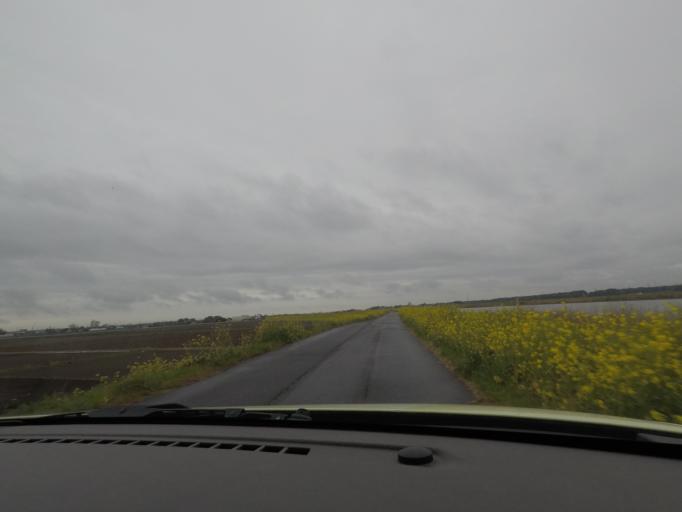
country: JP
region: Ibaraki
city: Mitsukaido
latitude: 36.0497
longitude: 140.0244
